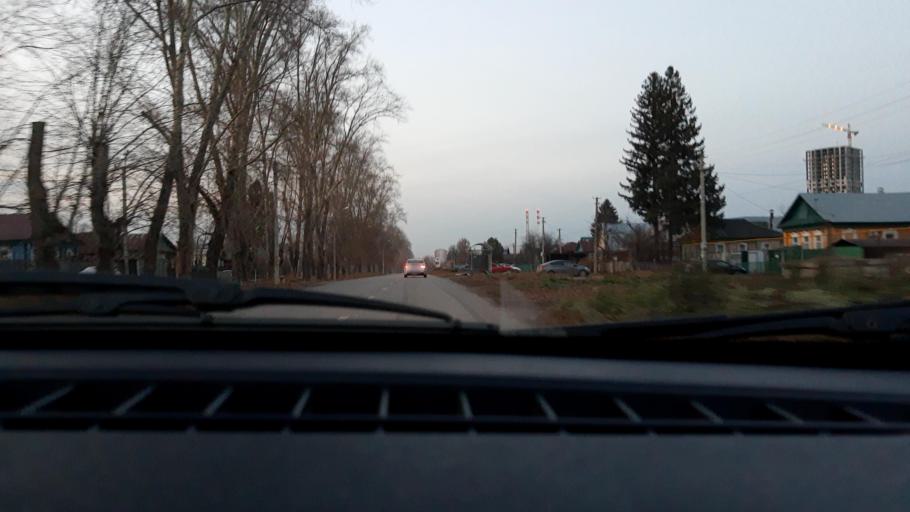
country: RU
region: Bashkortostan
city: Mikhaylovka
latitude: 54.7657
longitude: 55.8979
